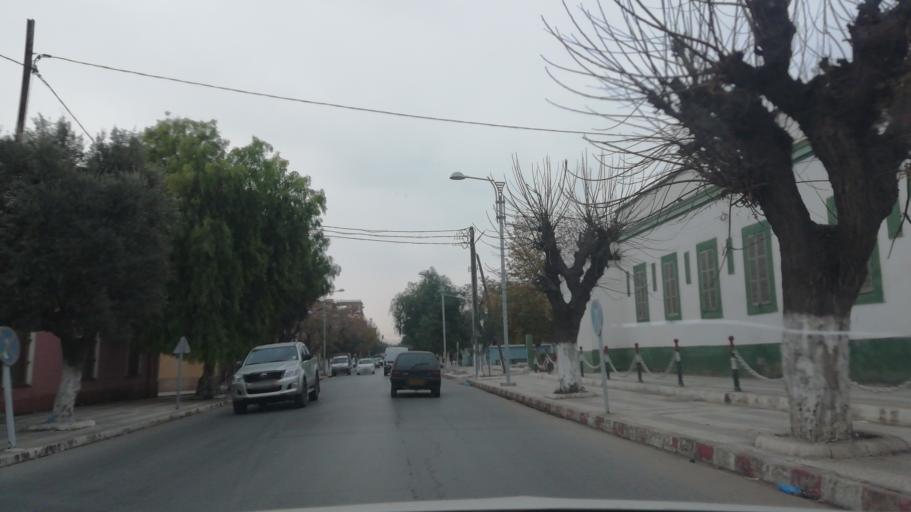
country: DZ
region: Sidi Bel Abbes
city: Sfizef
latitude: 35.2363
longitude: -0.2412
